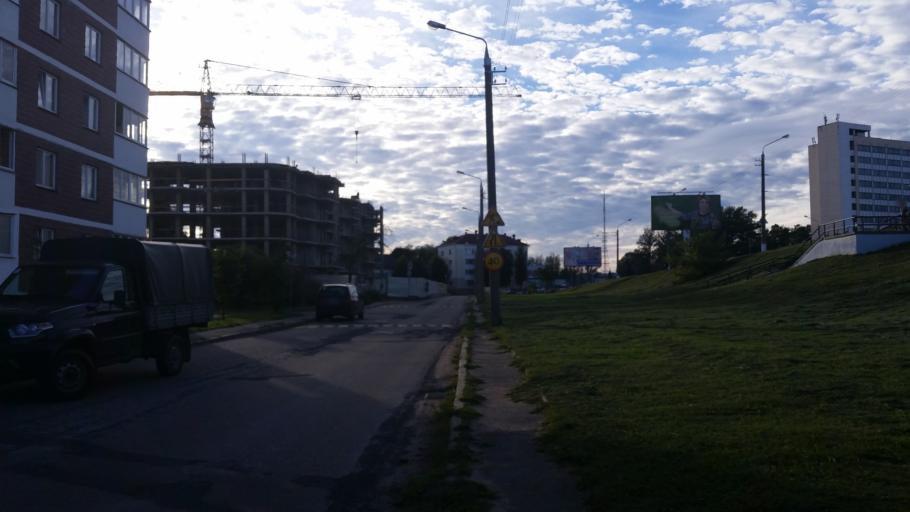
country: BY
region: Vitebsk
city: Vitebsk
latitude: 55.1841
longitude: 30.1943
